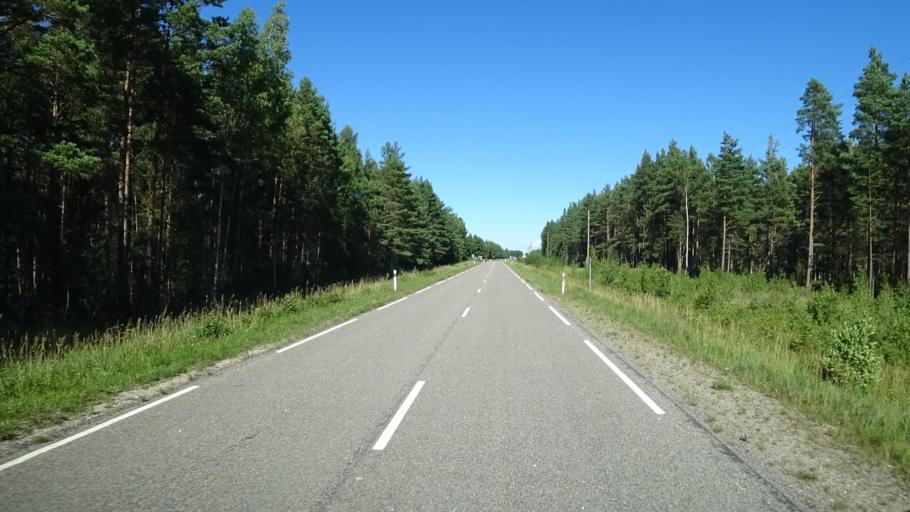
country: LV
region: Dundaga
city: Dundaga
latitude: 57.6930
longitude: 22.3931
